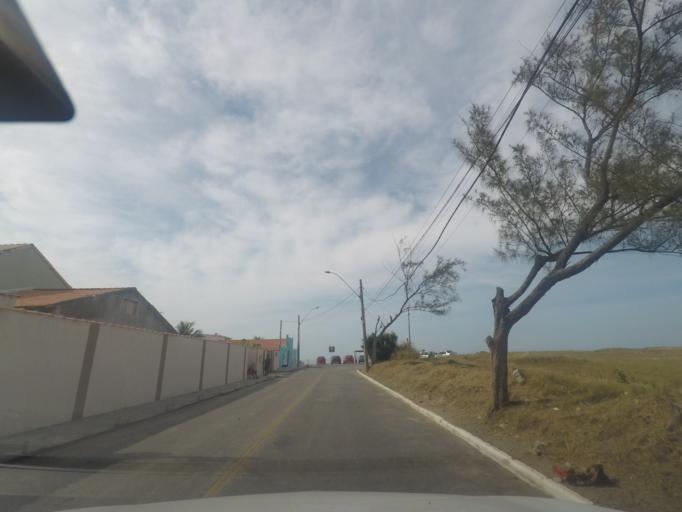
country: BR
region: Rio de Janeiro
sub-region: Marica
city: Marica
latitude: -22.9610
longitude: -42.8275
